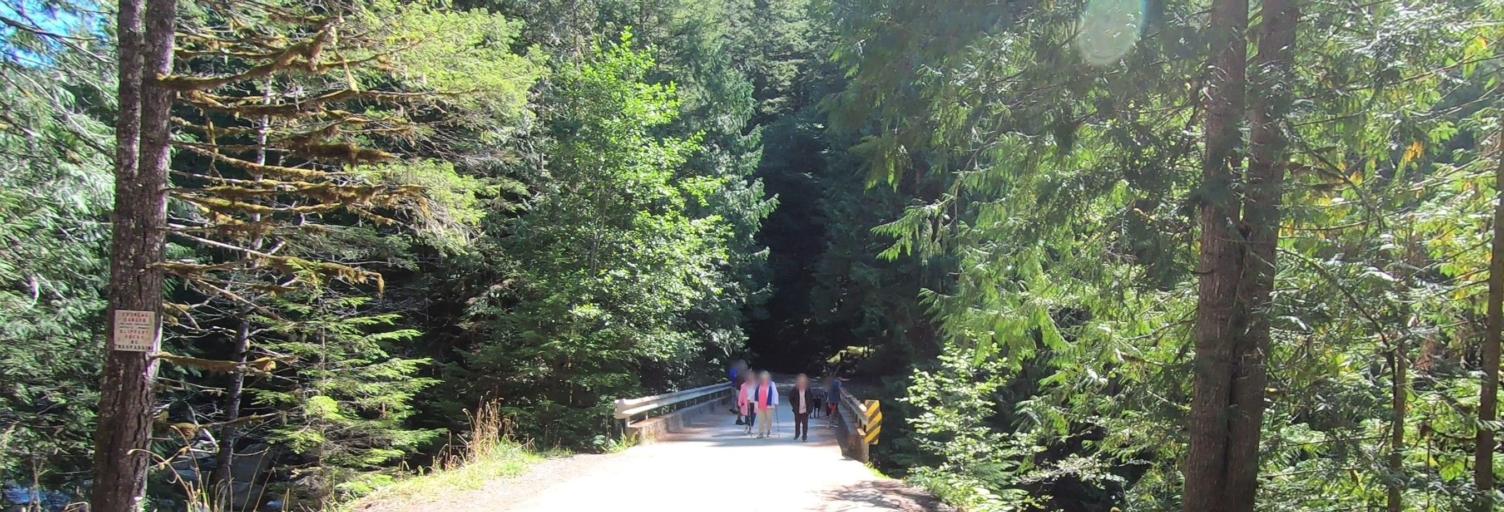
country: CA
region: British Columbia
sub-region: Fraser Valley Regional District
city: Chilliwack
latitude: 48.9057
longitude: -121.8087
